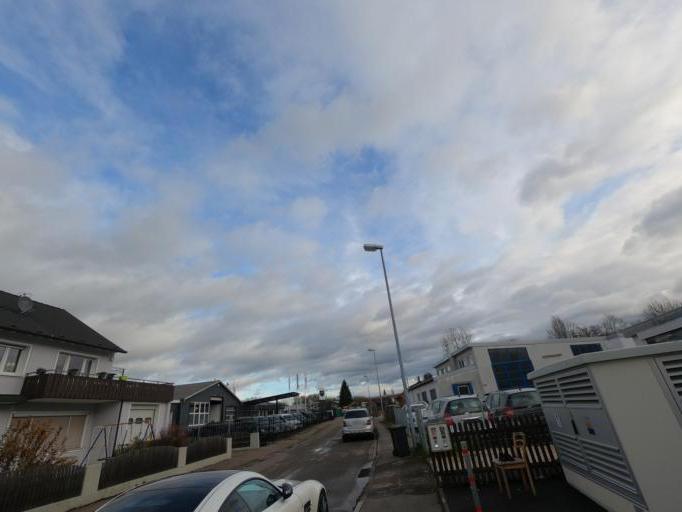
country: DE
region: Baden-Wuerttemberg
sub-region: Regierungsbezirk Stuttgart
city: Uhingen
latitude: 48.7045
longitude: 9.6019
